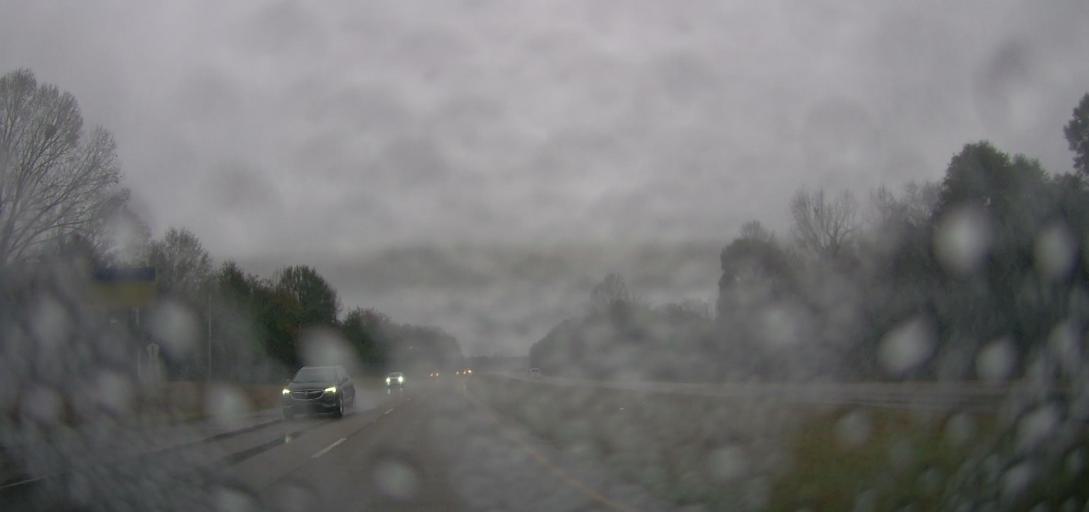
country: US
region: Alabama
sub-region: Autauga County
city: Prattville
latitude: 32.4325
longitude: -86.4179
